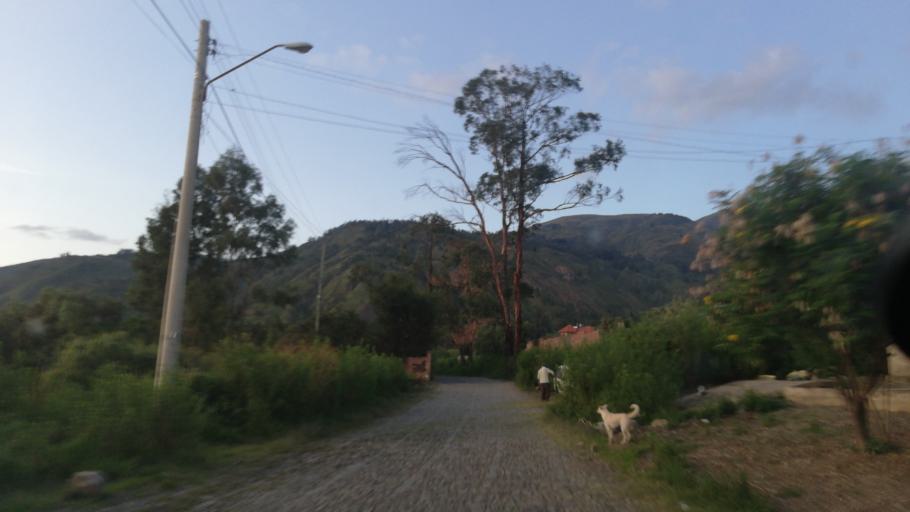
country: BO
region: Cochabamba
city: Cochabamba
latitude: -17.3258
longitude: -66.2076
